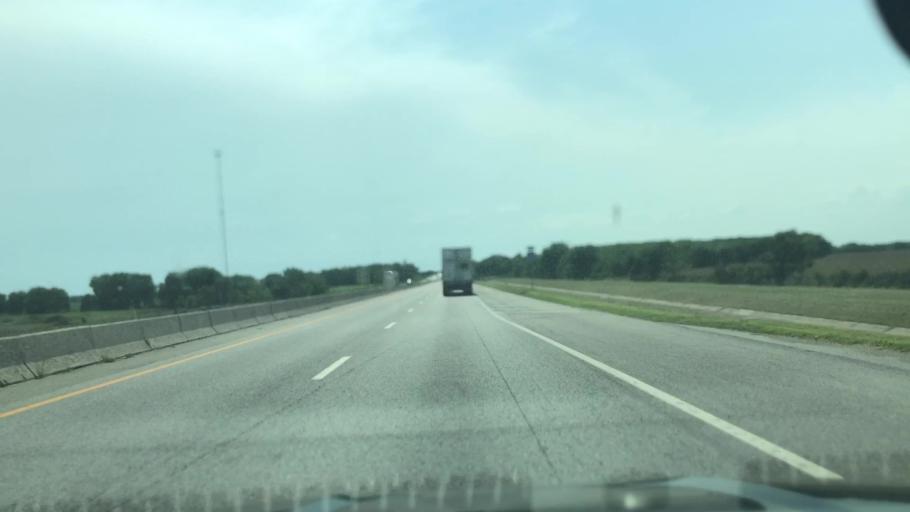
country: US
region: Oklahoma
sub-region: Ottawa County
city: Afton
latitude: 36.7215
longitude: -94.9380
